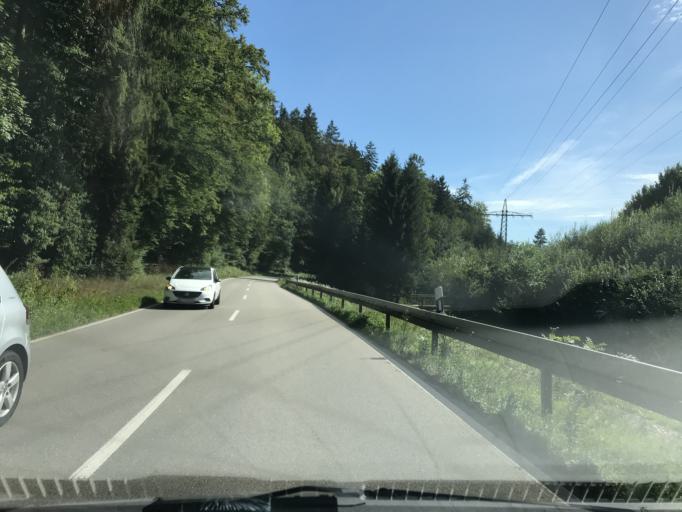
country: DE
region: Baden-Wuerttemberg
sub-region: Freiburg Region
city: Schworstadt
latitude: 47.5978
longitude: 7.8666
